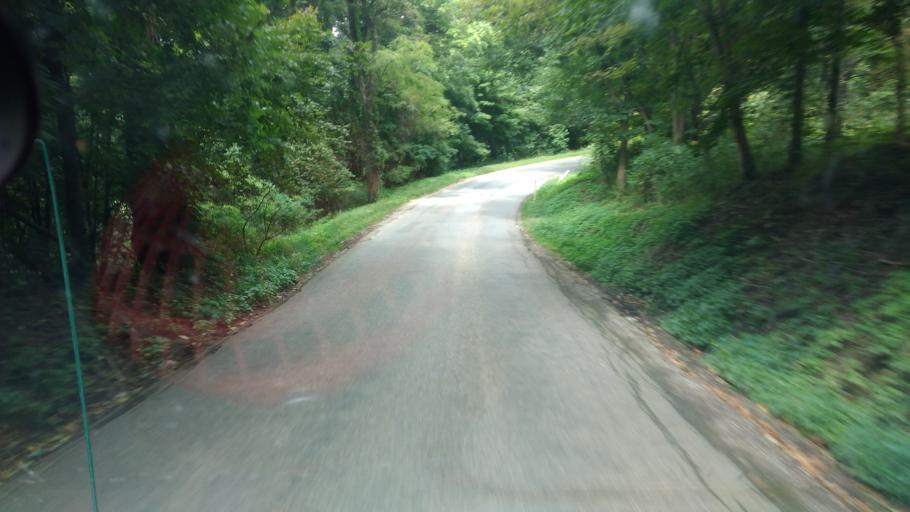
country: US
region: Ohio
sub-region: Ashland County
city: Ashland
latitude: 40.7770
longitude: -82.3642
